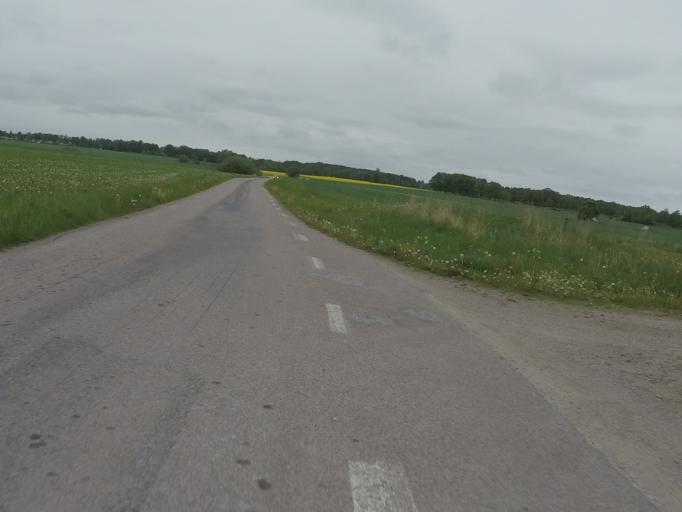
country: SE
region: Vaestmanland
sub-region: Hallstahammars Kommun
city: Kolback
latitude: 59.5503
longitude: 16.2809
